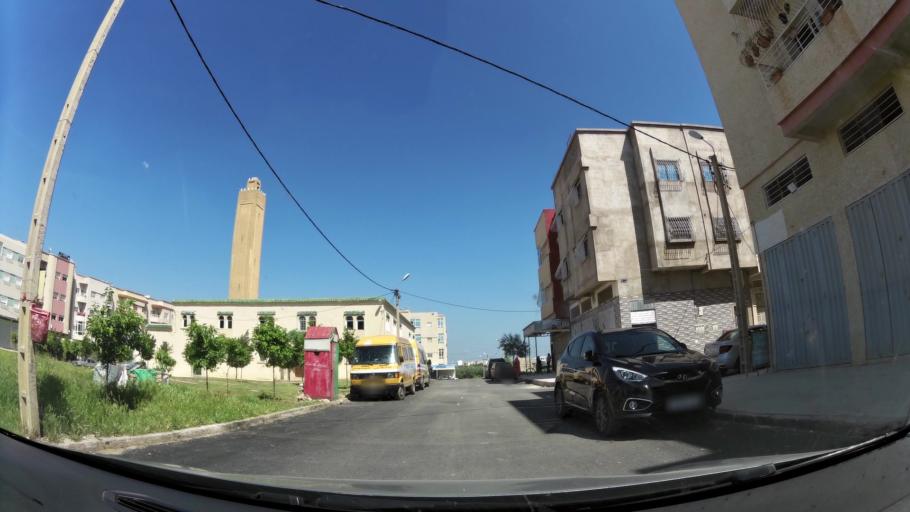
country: MA
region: Fes-Boulemane
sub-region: Fes
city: Fes
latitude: 34.0067
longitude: -5.0336
